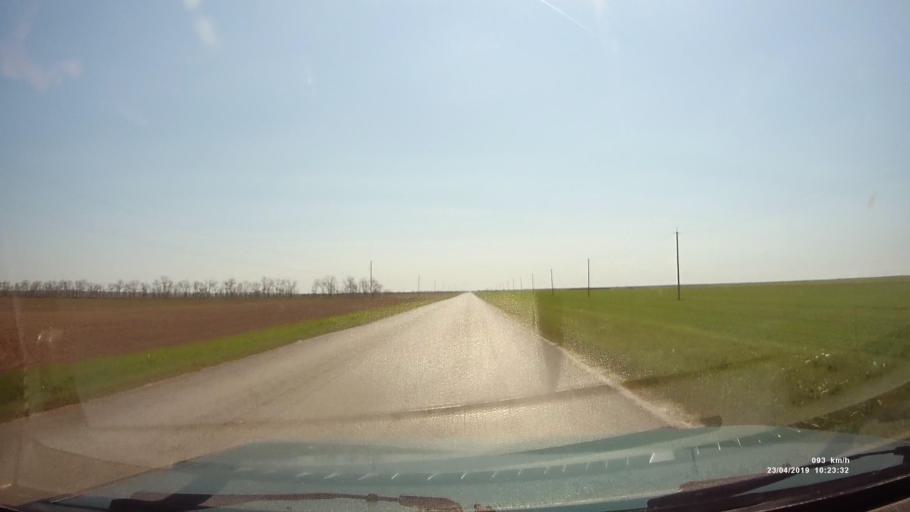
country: RU
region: Rostov
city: Sovetskoye
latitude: 46.6467
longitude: 42.4261
